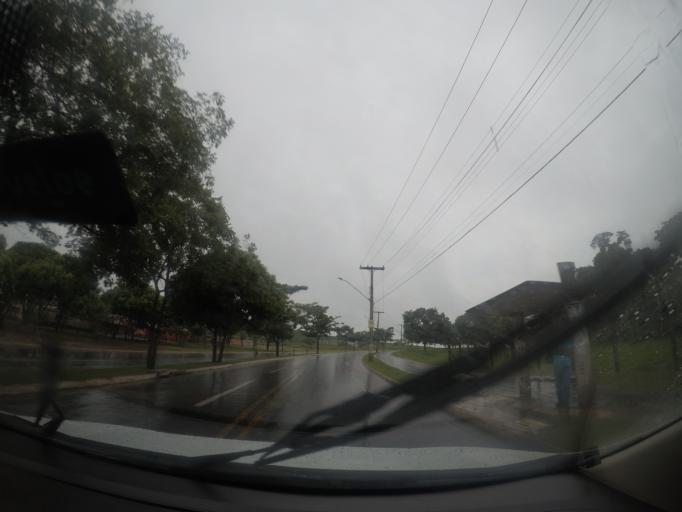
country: BR
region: Goias
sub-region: Goiania
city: Goiania
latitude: -16.6003
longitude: -49.3307
